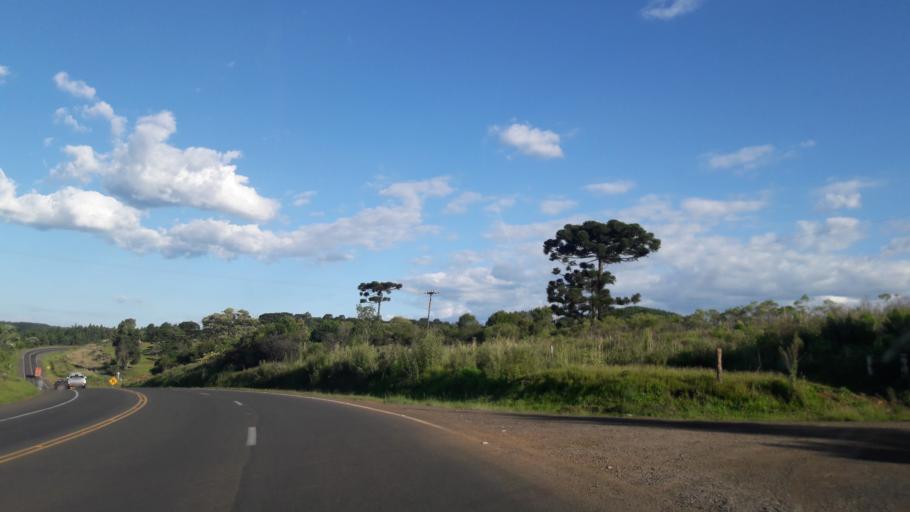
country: BR
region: Parana
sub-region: Guarapuava
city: Guarapuava
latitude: -25.3658
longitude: -51.3485
